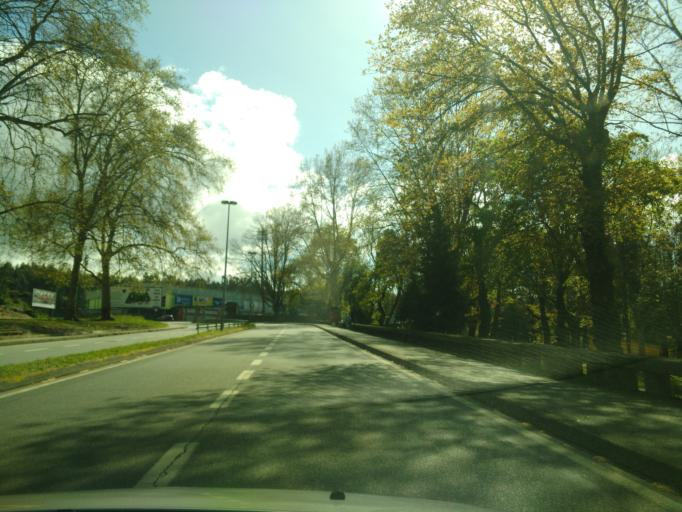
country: PT
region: Braga
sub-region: Braga
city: Braga
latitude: 41.5414
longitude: -8.4183
